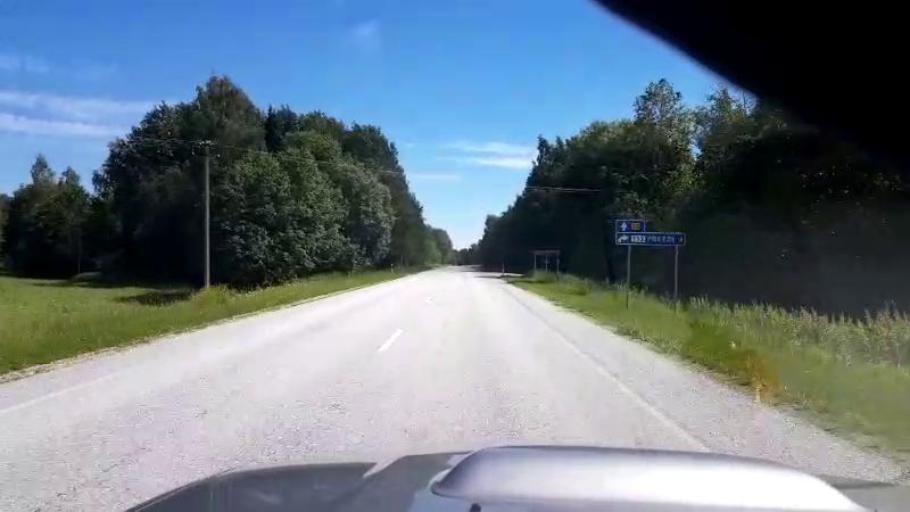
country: EE
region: Laeaene-Virumaa
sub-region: Rakke vald
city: Rakke
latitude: 58.9505
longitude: 26.1797
